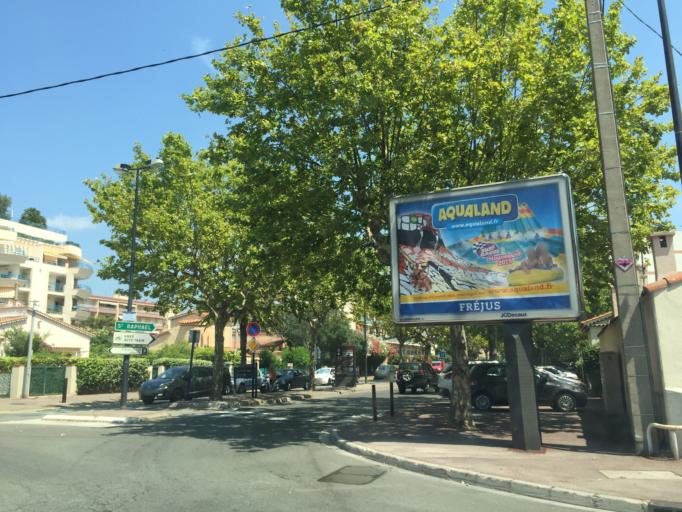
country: FR
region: Provence-Alpes-Cote d'Azur
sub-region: Departement du Var
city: Saint-Raphael
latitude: 43.4264
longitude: 6.7559
